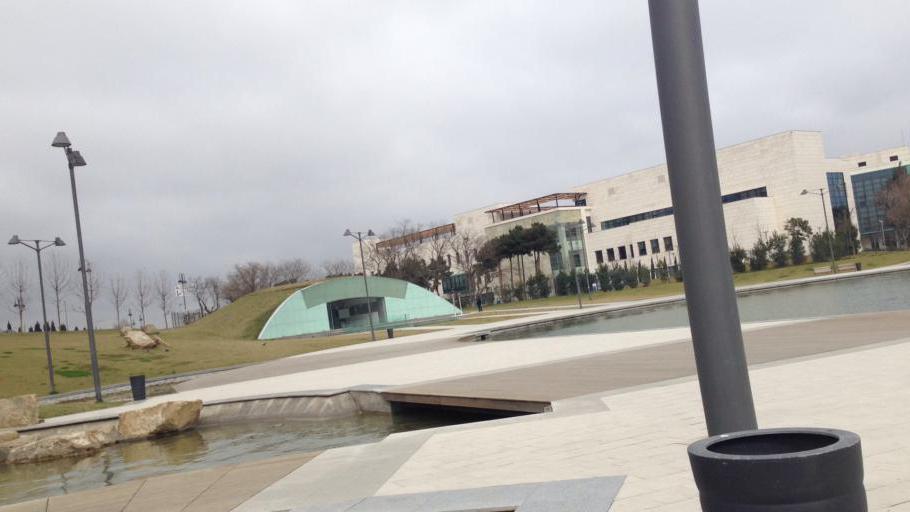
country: AZ
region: Baki
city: Baku
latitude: 40.3934
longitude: 49.8471
